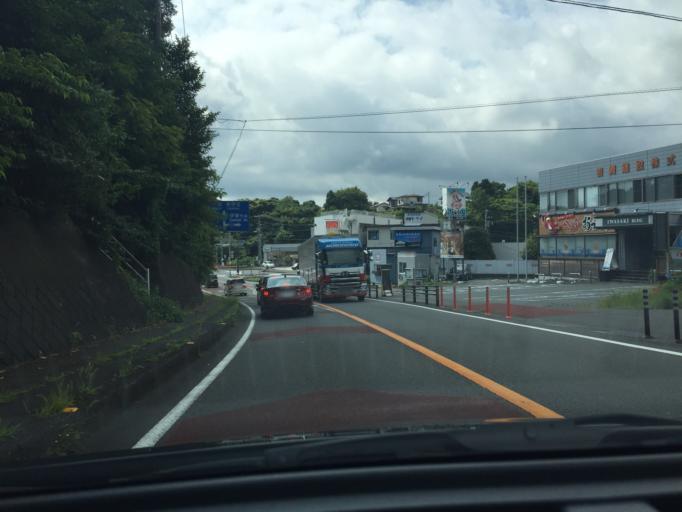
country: JP
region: Shizuoka
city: Ito
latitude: 34.9546
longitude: 139.1164
